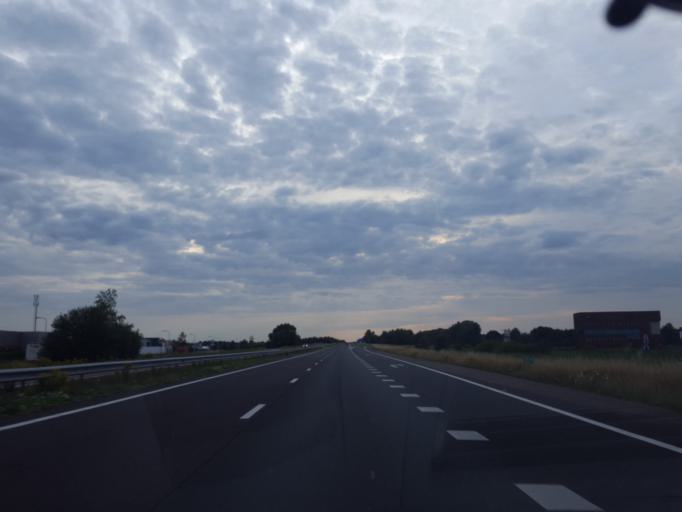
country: NL
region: Overijssel
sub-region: Gemeente Steenwijkerland
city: Steenwijk
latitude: 52.7977
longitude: 6.1354
